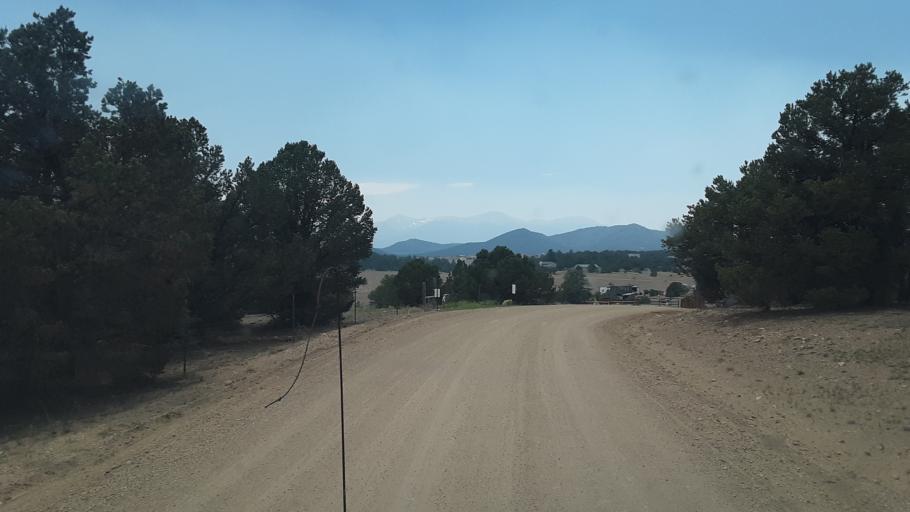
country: US
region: Colorado
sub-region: Custer County
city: Westcliffe
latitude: 38.2916
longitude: -105.4901
